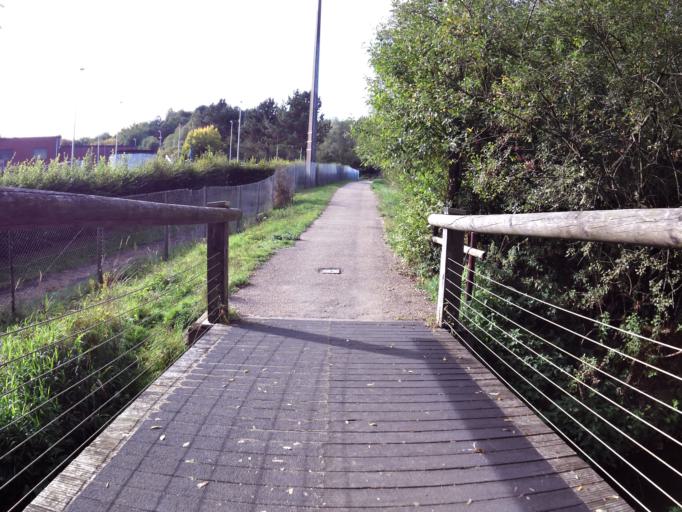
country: BE
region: Wallonia
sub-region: Province de Liege
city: Saint-Vith
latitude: 50.2736
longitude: 6.1375
